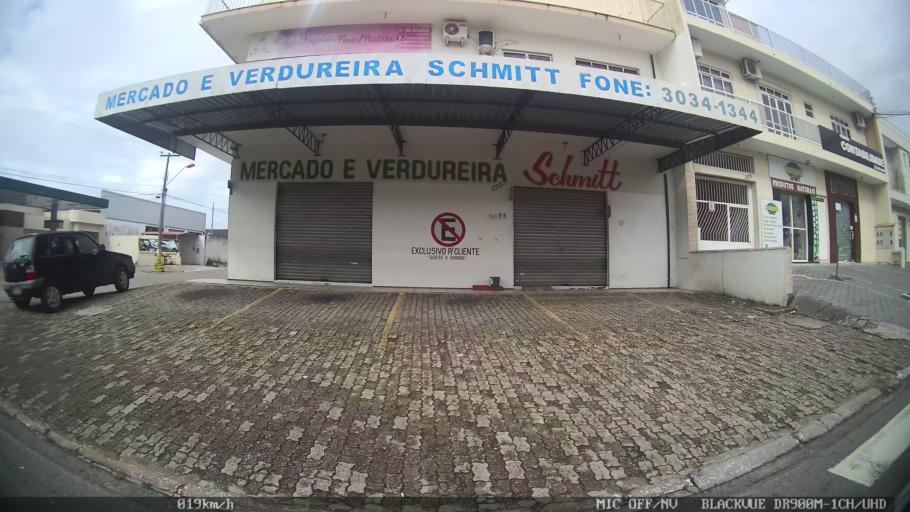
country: BR
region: Santa Catarina
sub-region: Sao Jose
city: Campinas
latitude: -27.5610
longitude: -48.6191
